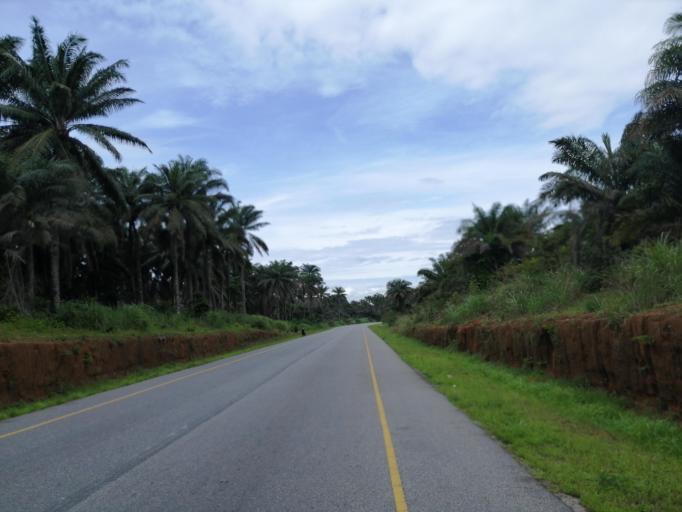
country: SL
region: Northern Province
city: Port Loko
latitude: 8.7610
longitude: -12.9097
